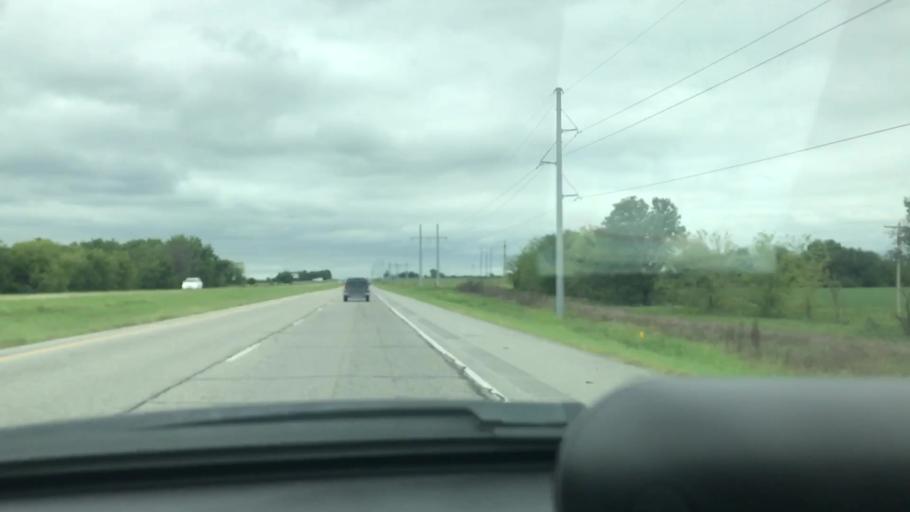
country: US
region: Oklahoma
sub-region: Wagoner County
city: Wagoner
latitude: 36.0044
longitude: -95.3686
